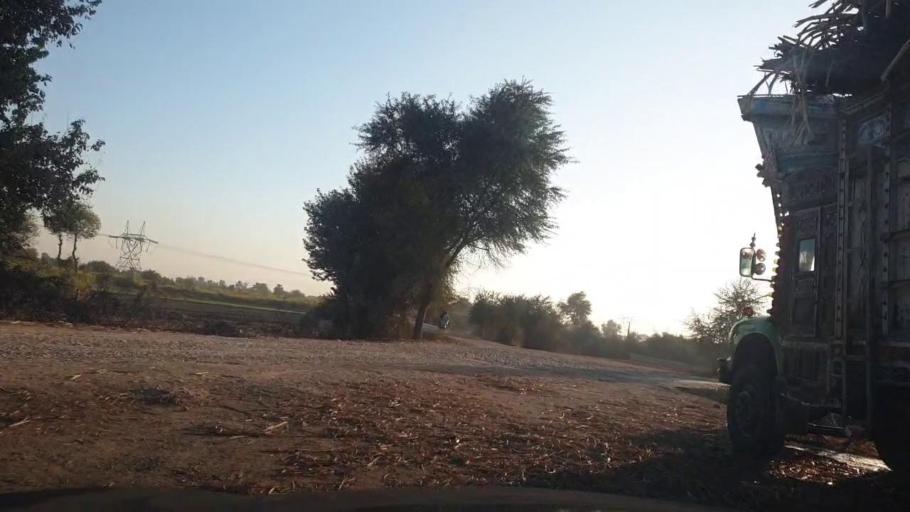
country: PK
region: Sindh
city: Mirpur Mathelo
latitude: 27.9885
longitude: 69.4645
